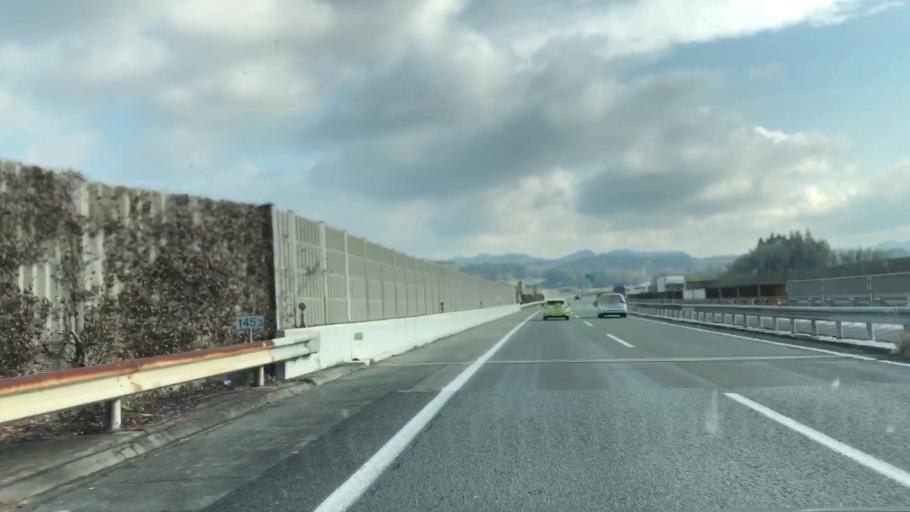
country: JP
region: Kumamoto
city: Tamana
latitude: 32.9969
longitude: 130.5956
